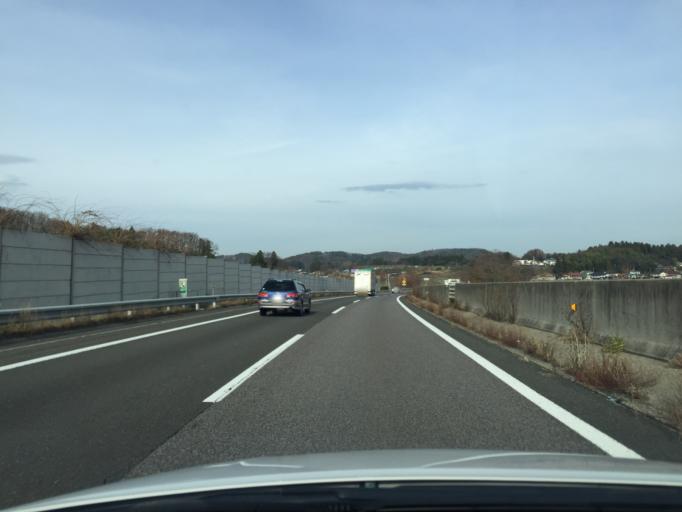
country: JP
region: Fukushima
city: Nihommatsu
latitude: 37.6074
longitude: 140.4215
